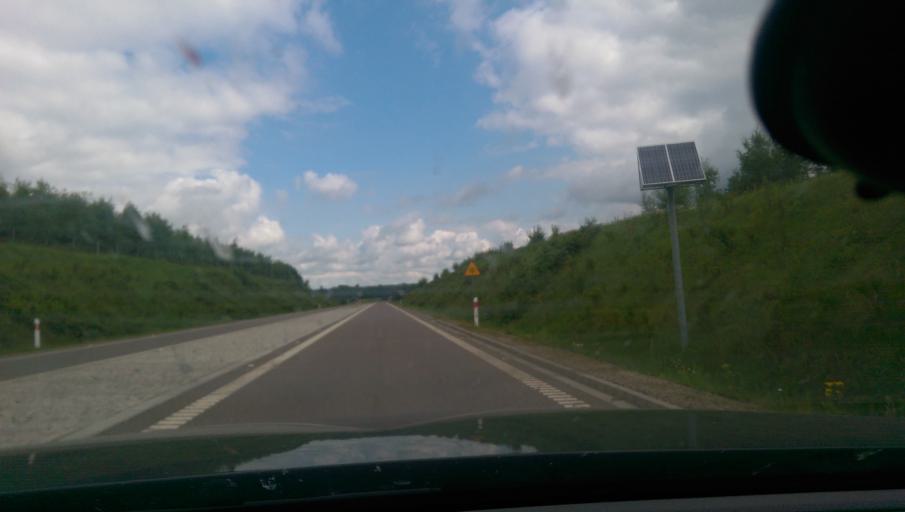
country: PL
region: Warmian-Masurian Voivodeship
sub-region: Powiat goldapski
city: Goldap
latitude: 54.3071
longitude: 22.2797
